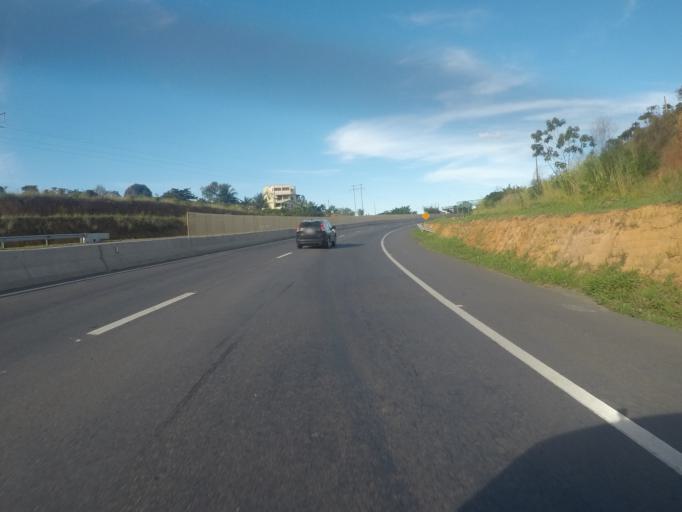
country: BR
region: Espirito Santo
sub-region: Ibiracu
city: Ibiracu
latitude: -19.8639
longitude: -40.3914
